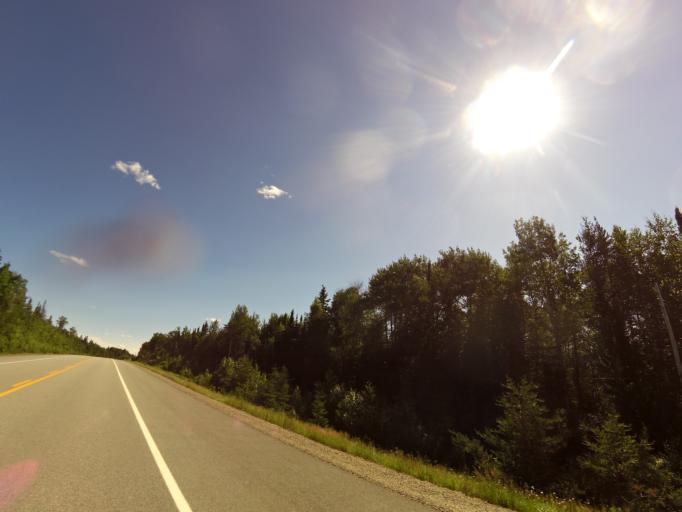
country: CA
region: Quebec
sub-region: Abitibi-Temiscamingue
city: Val-d'Or
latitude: 47.8842
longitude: -77.3459
